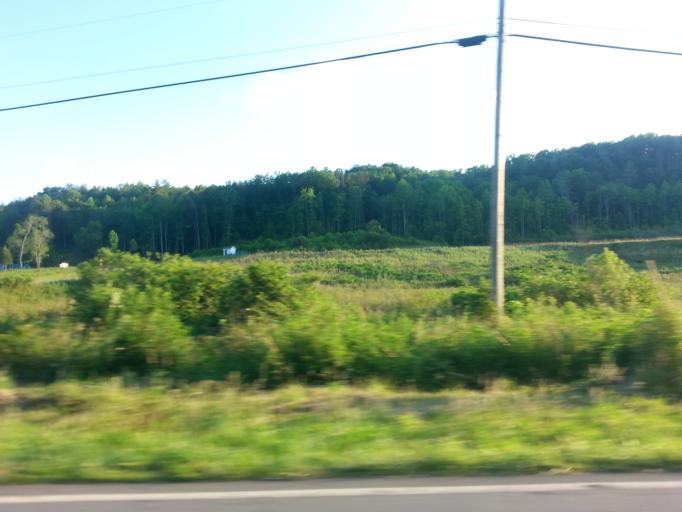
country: US
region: North Carolina
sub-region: Cherokee County
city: Murphy
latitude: 35.1062
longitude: -84.2238
